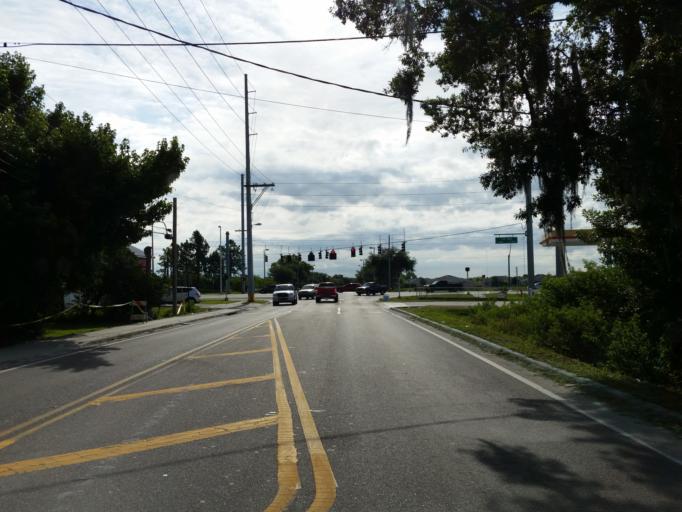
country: US
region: Florida
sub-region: Hillsborough County
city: Riverview
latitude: 27.8352
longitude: -82.3297
